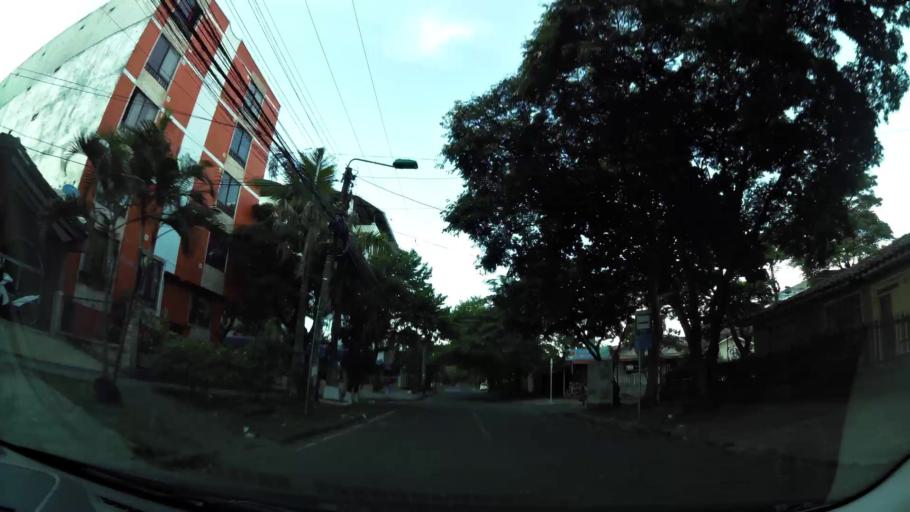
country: CO
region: Valle del Cauca
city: Cali
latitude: 3.4049
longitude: -76.5497
